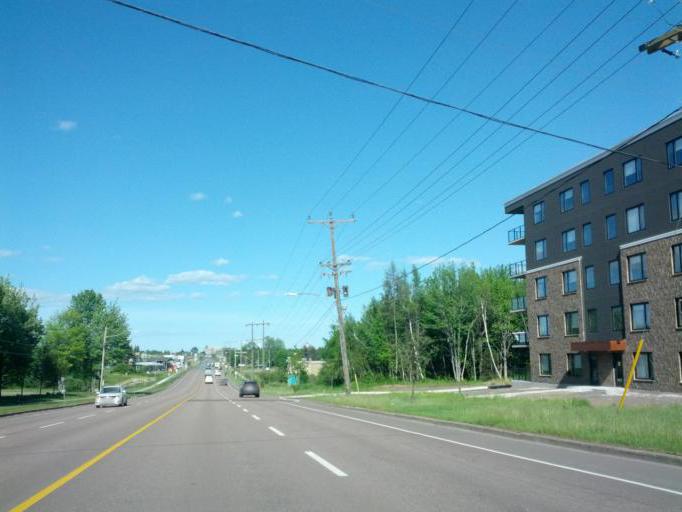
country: CA
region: New Brunswick
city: Moncton
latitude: 46.0837
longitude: -64.8176
